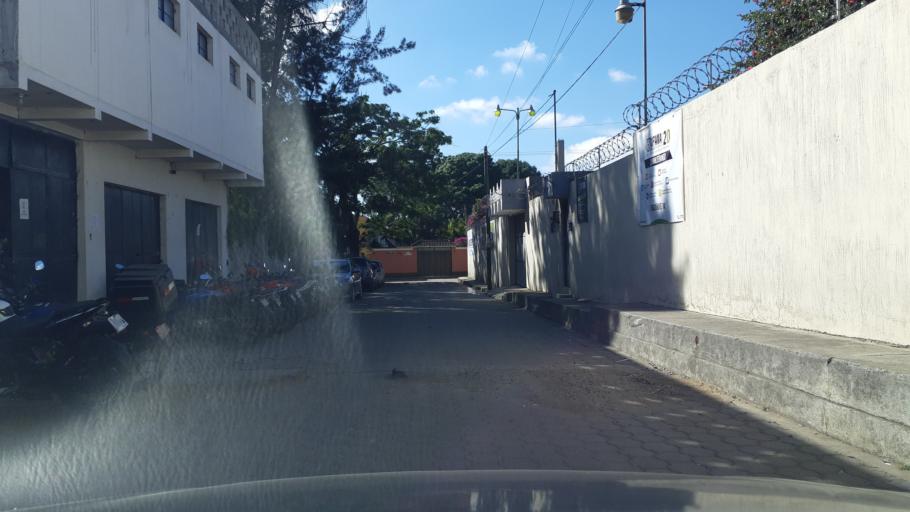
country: GT
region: Chimaltenango
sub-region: Municipio de Chimaltenango
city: Chimaltenango
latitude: 14.6534
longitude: -90.8177
